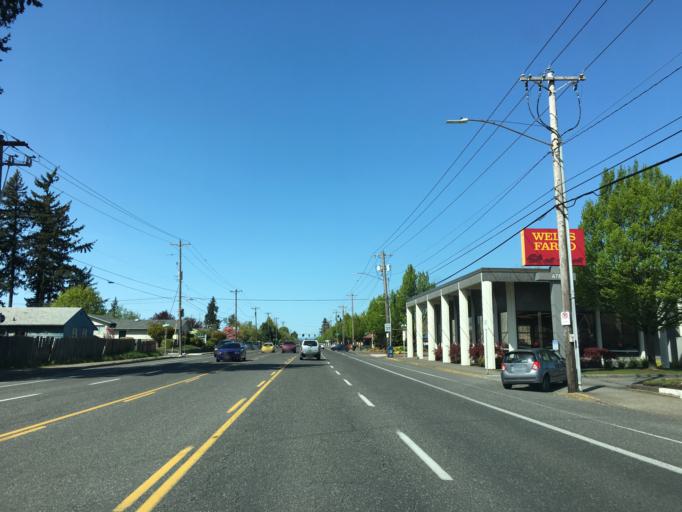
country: US
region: Oregon
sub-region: Multnomah County
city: Lents
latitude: 45.5343
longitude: -122.5376
